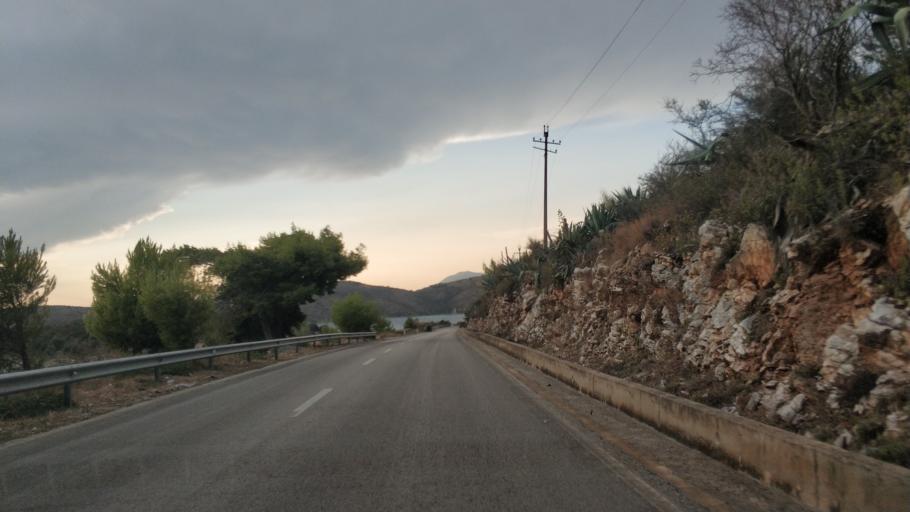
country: AL
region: Vlore
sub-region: Rrethi i Vlores
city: Himare
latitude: 40.0610
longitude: 19.7970
